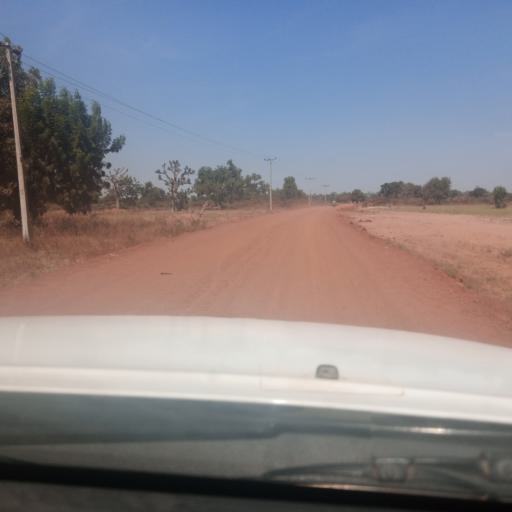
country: NG
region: Adamawa
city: Yola
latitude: 9.2034
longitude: 12.8774
